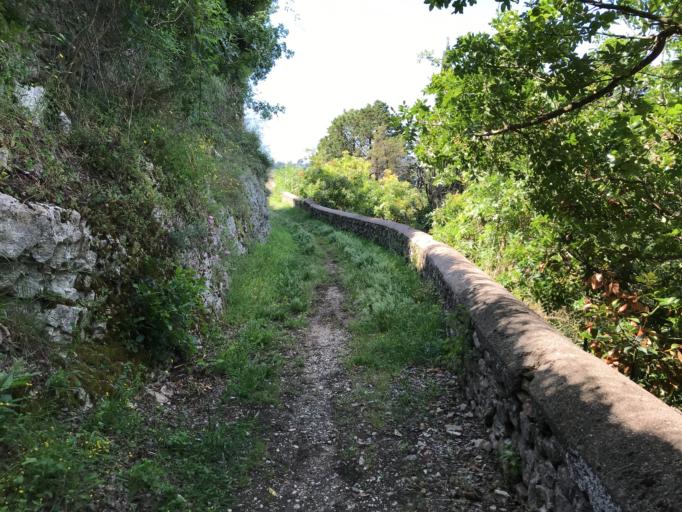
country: IT
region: Umbria
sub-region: Provincia di Terni
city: Amelia
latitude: 42.5554
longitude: 12.4127
